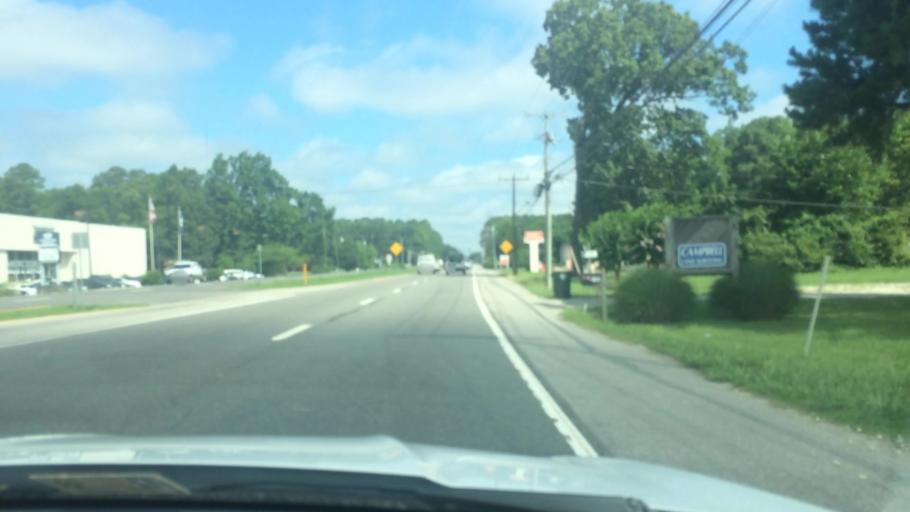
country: US
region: Virginia
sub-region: York County
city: Yorktown
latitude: 37.1816
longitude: -76.4823
